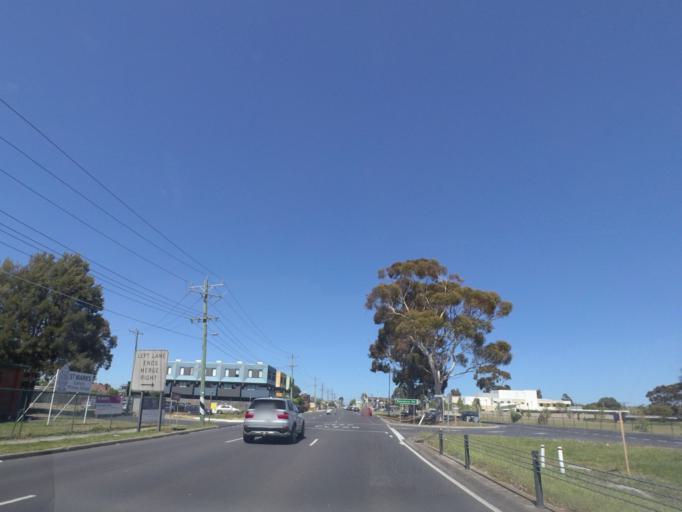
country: AU
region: Victoria
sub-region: Moreland
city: Fawkner
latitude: -37.7165
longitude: 144.9626
